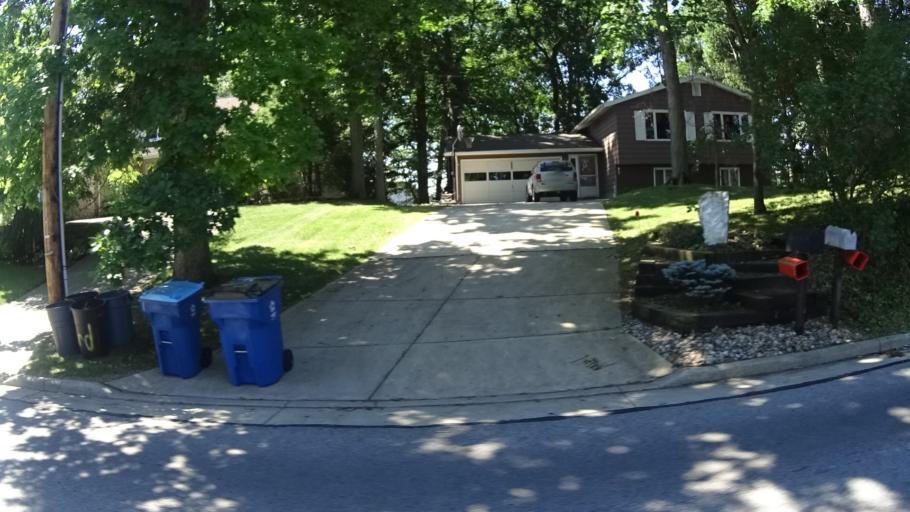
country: US
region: Ohio
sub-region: Erie County
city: Huron
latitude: 41.3766
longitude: -82.5591
